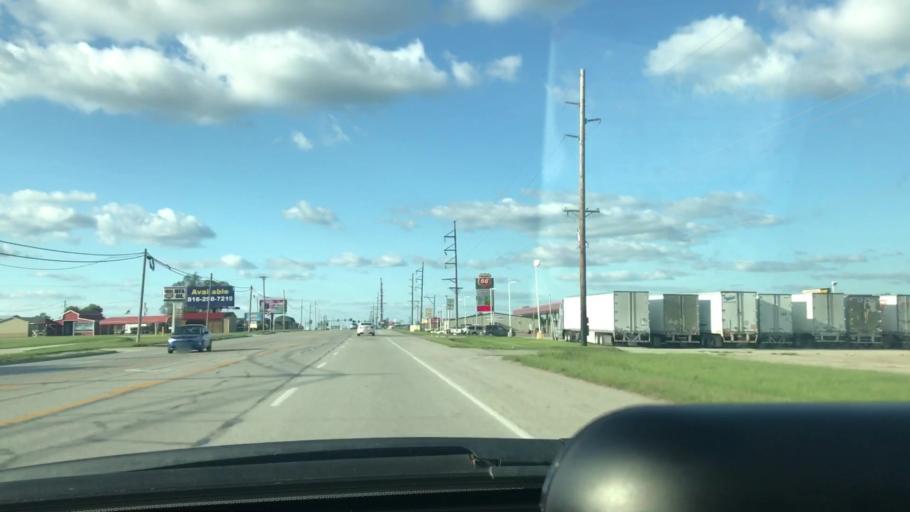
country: US
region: Missouri
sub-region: Pettis County
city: Sedalia
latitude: 38.6705
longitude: -93.2518
